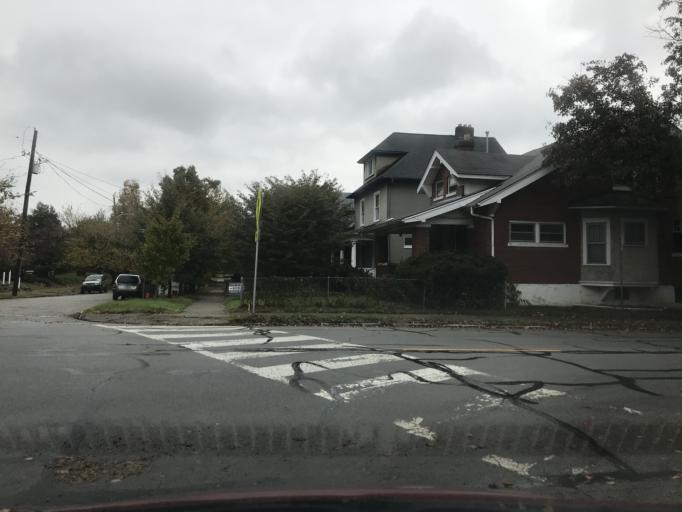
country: US
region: Kentucky
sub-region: Jefferson County
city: Audubon Park
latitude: 38.2338
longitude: -85.7190
